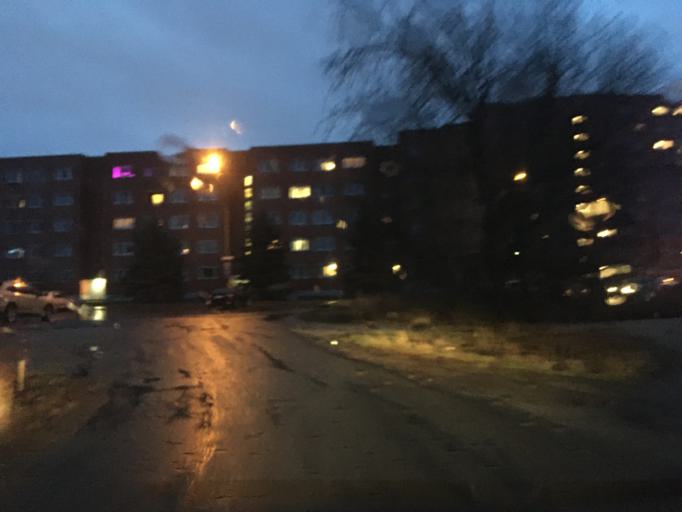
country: EE
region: Harju
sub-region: Tallinna linn
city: Tallinn
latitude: 59.4402
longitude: 24.8120
